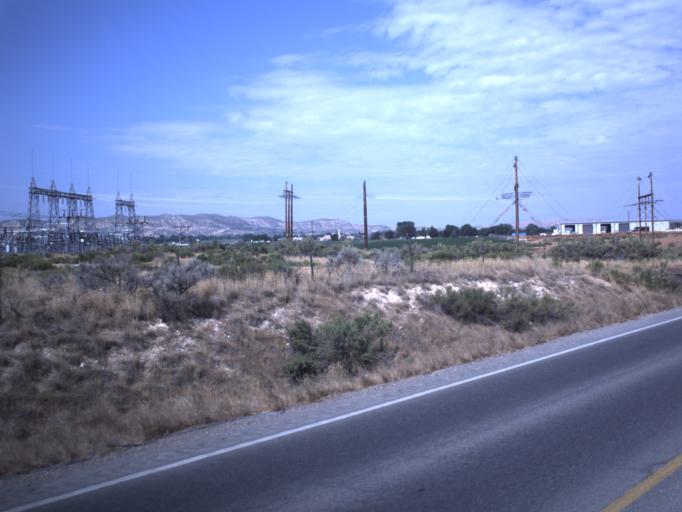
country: US
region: Utah
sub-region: Uintah County
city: Naples
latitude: 40.3985
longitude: -109.4623
